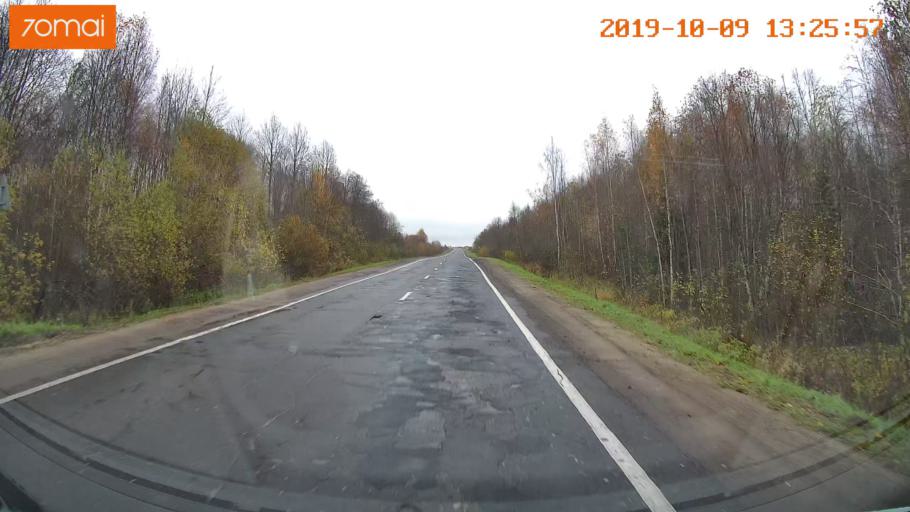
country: RU
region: Jaroslavl
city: Lyubim
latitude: 58.3244
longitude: 40.9184
